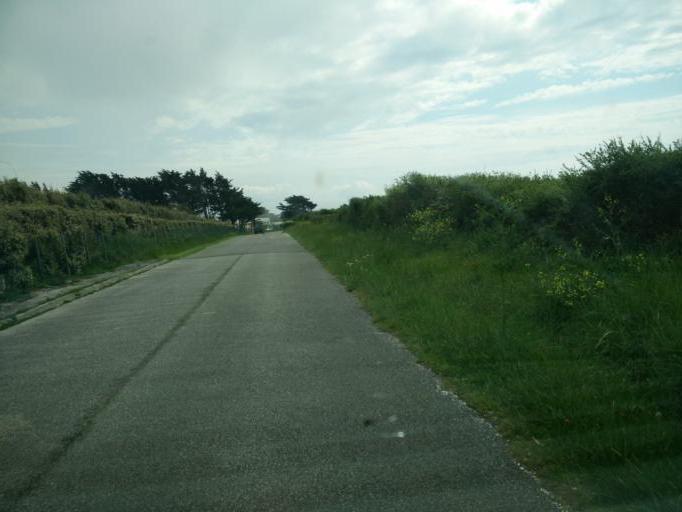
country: FR
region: Brittany
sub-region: Departement du Finistere
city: Camaret-sur-Mer
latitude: 48.2776
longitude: -4.6088
